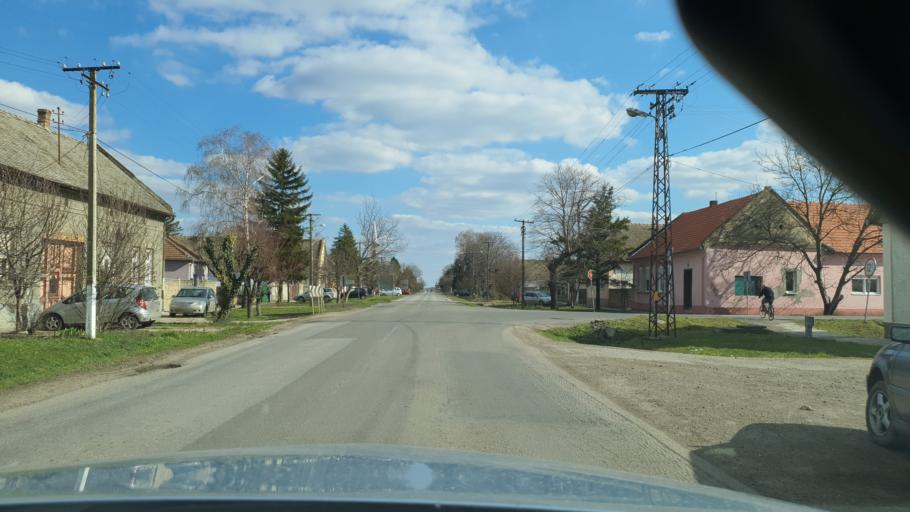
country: RS
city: Zmajevo
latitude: 45.4502
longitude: 19.6938
